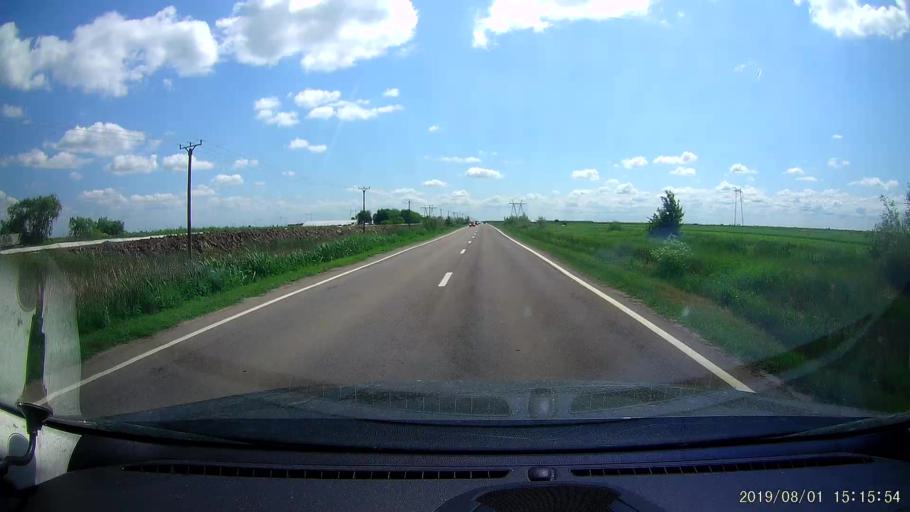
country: RO
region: Braila
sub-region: Comuna Tichilesti
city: Tichilesti
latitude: 45.1571
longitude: 27.8618
